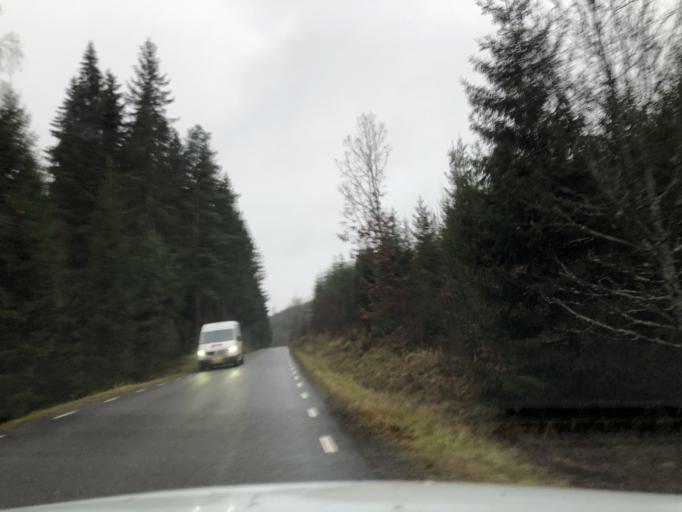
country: SE
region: Vaestra Goetaland
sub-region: Ulricehamns Kommun
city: Ulricehamn
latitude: 57.8307
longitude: 13.4083
